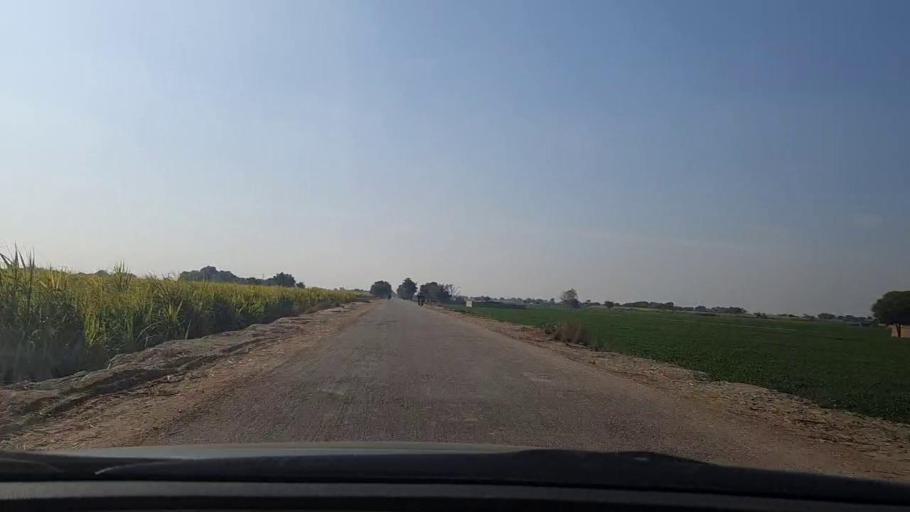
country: PK
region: Sindh
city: Daulatpur
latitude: 26.3205
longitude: 68.0348
